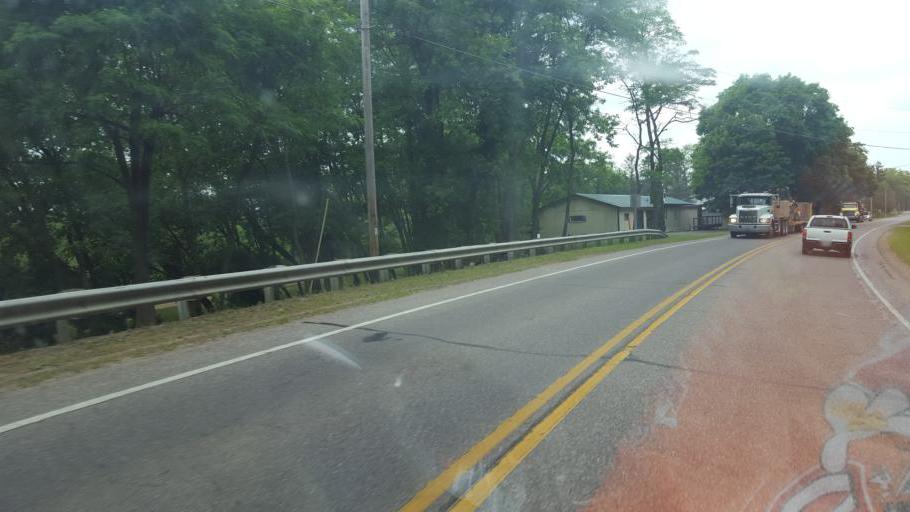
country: US
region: Wisconsin
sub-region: Juneau County
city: Elroy
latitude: 43.6426
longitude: -90.2173
